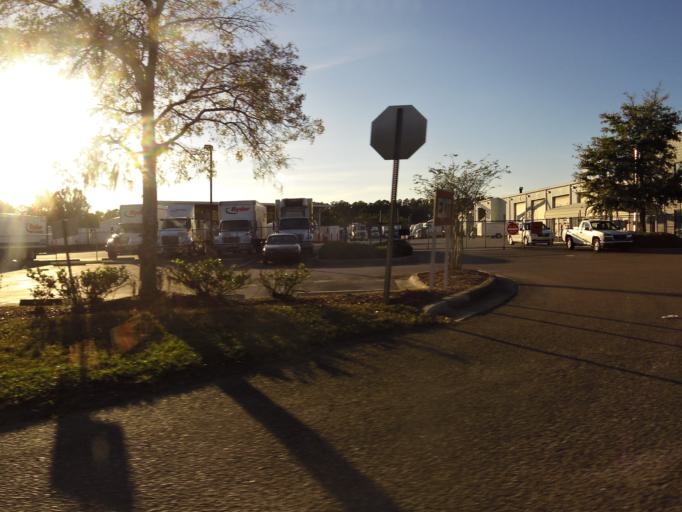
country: US
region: Florida
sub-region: Duval County
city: Jacksonville
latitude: 30.3341
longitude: -81.7647
